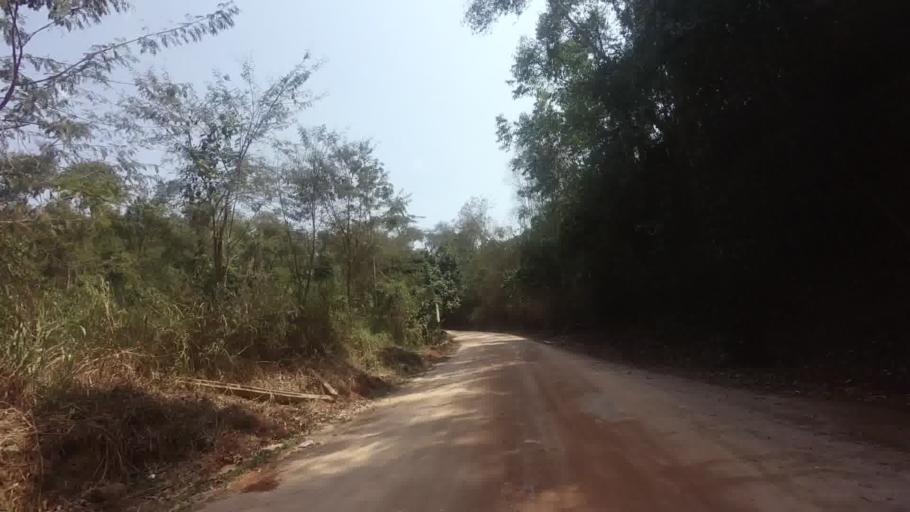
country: BR
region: Espirito Santo
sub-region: Mimoso Do Sul
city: Mimoso do Sul
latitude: -20.9441
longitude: -41.4006
